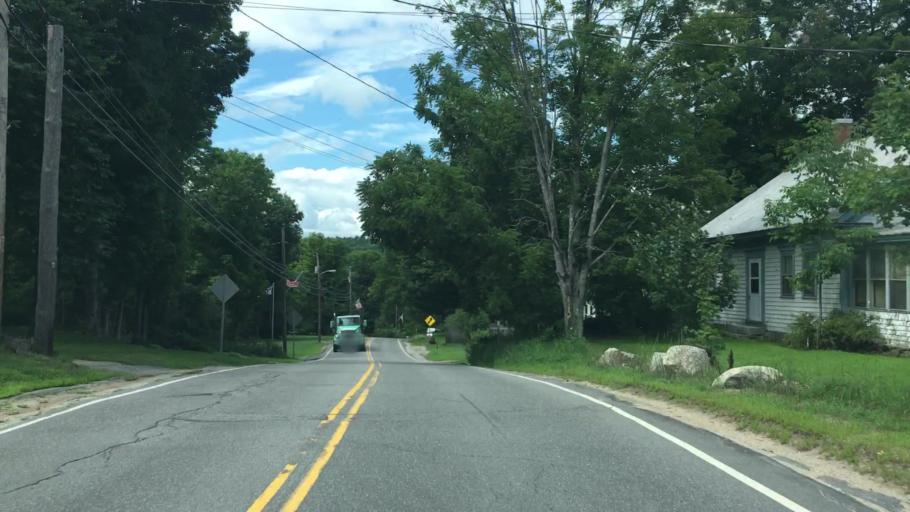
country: US
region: New Hampshire
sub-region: Belknap County
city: Meredith
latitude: 43.6141
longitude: -71.5302
